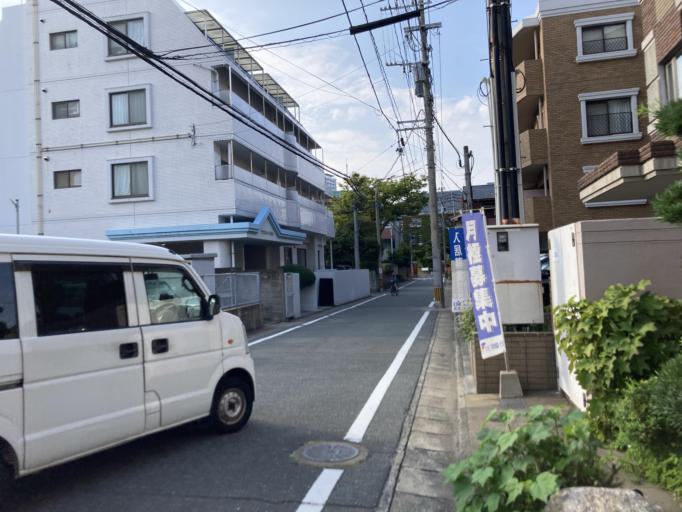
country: JP
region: Fukuoka
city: Fukuoka-shi
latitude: 33.5844
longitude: 130.3582
